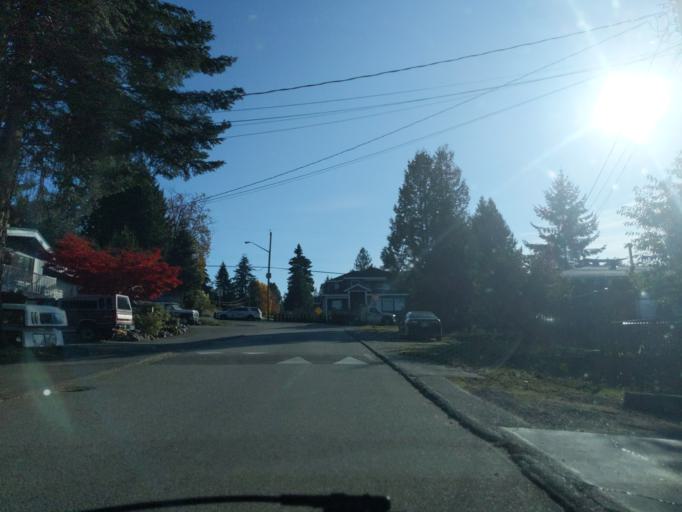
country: CA
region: British Columbia
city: New Westminster
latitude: 49.1995
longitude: -122.8648
